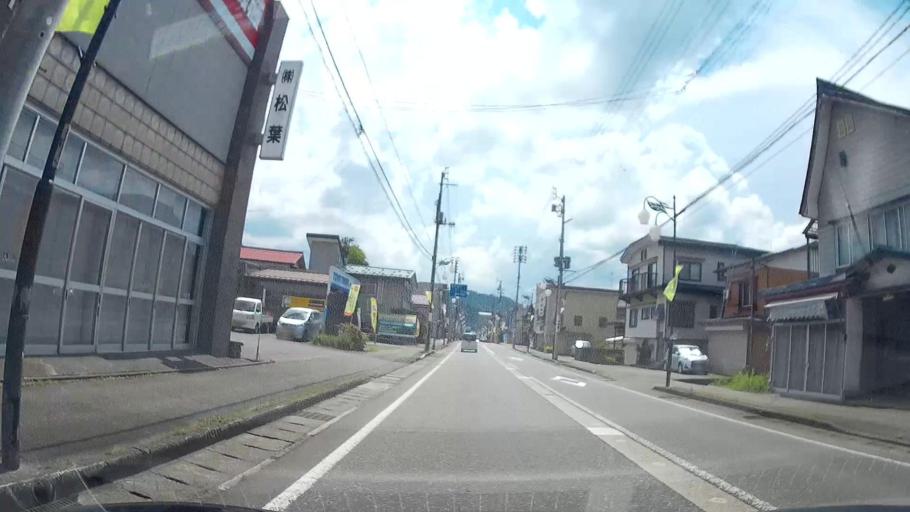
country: JP
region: Niigata
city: Tokamachi
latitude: 37.0162
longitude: 138.6538
